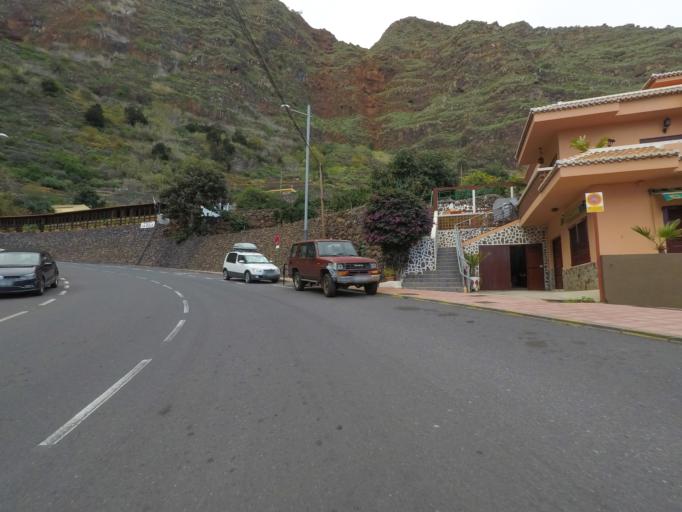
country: ES
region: Canary Islands
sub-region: Provincia de Santa Cruz de Tenerife
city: Agulo
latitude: 28.1868
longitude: -17.1962
